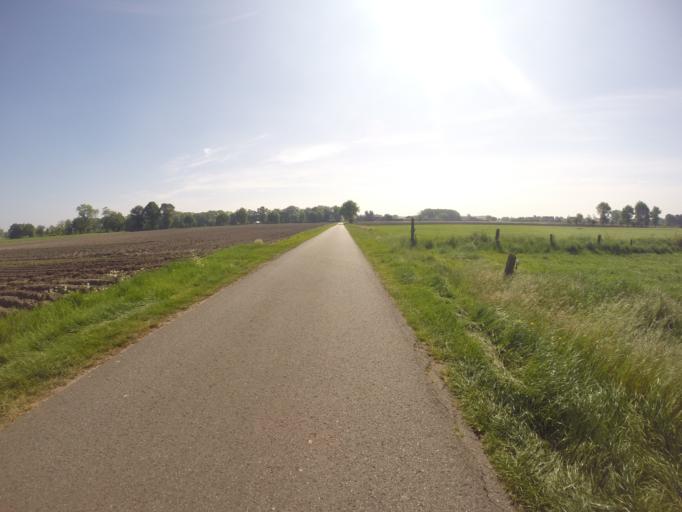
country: BE
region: Flanders
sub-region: Provincie West-Vlaanderen
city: Beernem
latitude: 51.1427
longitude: 3.3667
